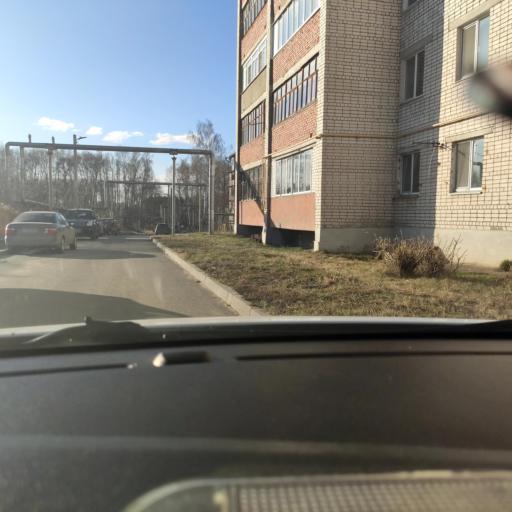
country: RU
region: Tatarstan
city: Vysokaya Gora
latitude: 55.8848
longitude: 49.2692
